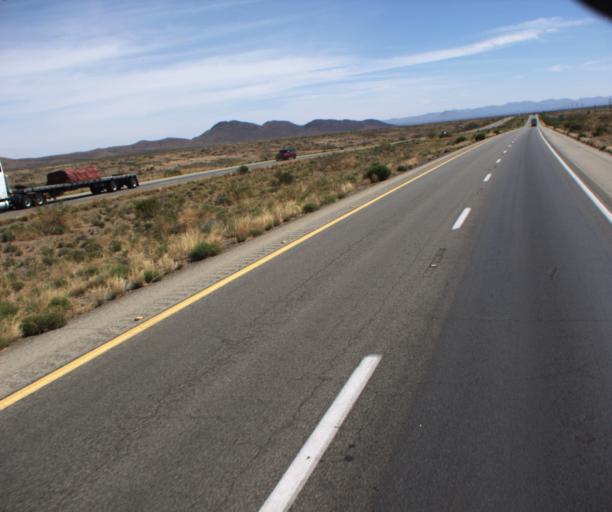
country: US
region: Arizona
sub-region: Cochise County
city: Willcox
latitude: 32.3624
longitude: -109.6472
